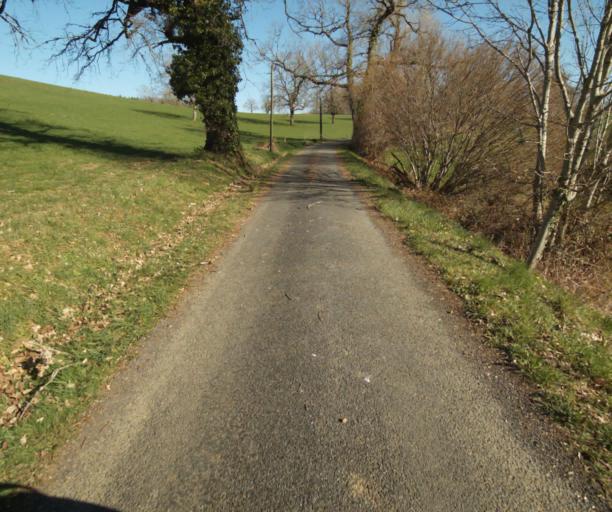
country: FR
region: Limousin
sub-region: Departement de la Correze
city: Seilhac
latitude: 45.3824
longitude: 1.7595
